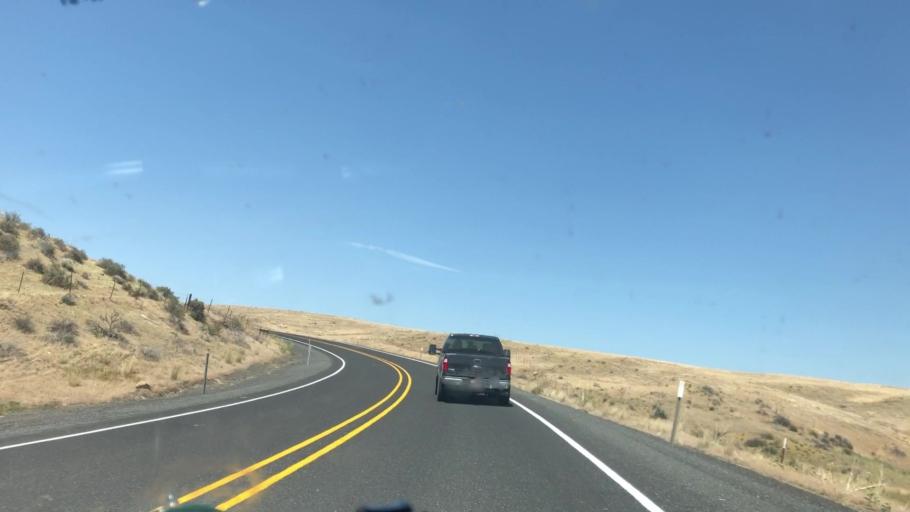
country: US
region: Idaho
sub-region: Owyhee County
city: Marsing
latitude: 43.2322
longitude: -117.0464
